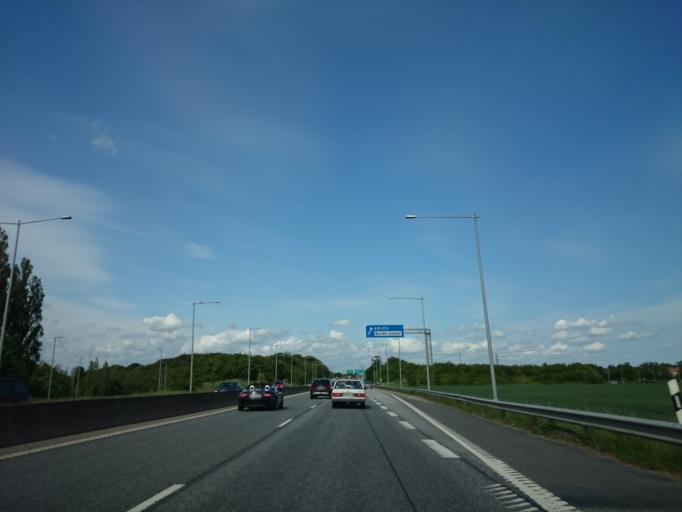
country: SE
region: Skane
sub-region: Burlovs Kommun
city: Arloev
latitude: 55.6344
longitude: 13.0914
